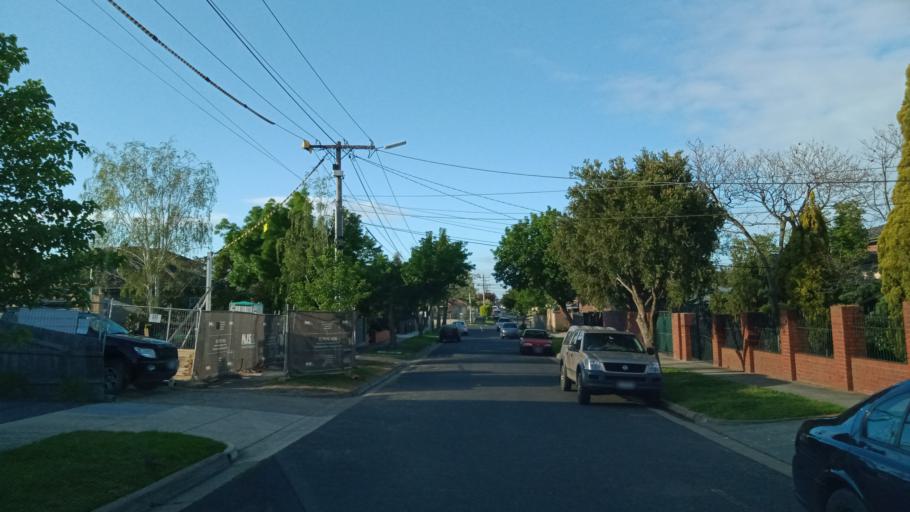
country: AU
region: Victoria
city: McKinnon
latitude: -37.9283
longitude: 145.0551
